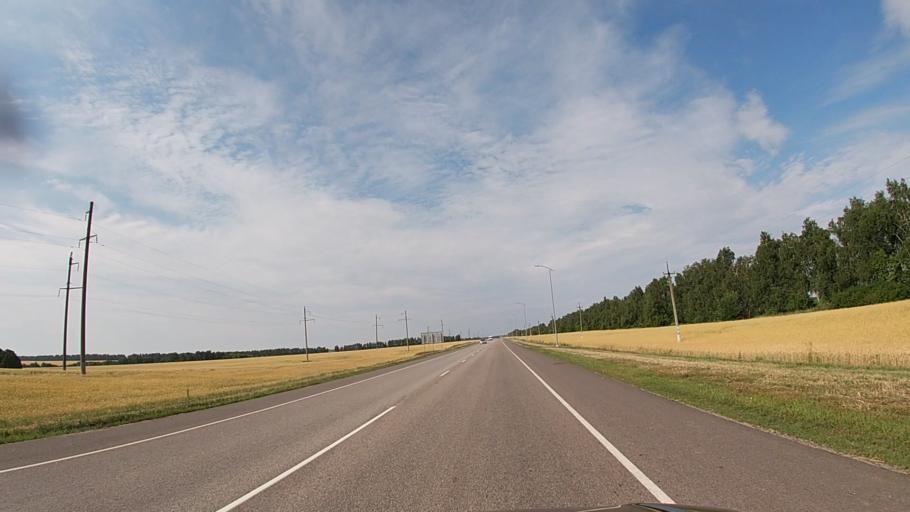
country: RU
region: Belgorod
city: Proletarskiy
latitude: 50.8294
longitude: 35.7643
